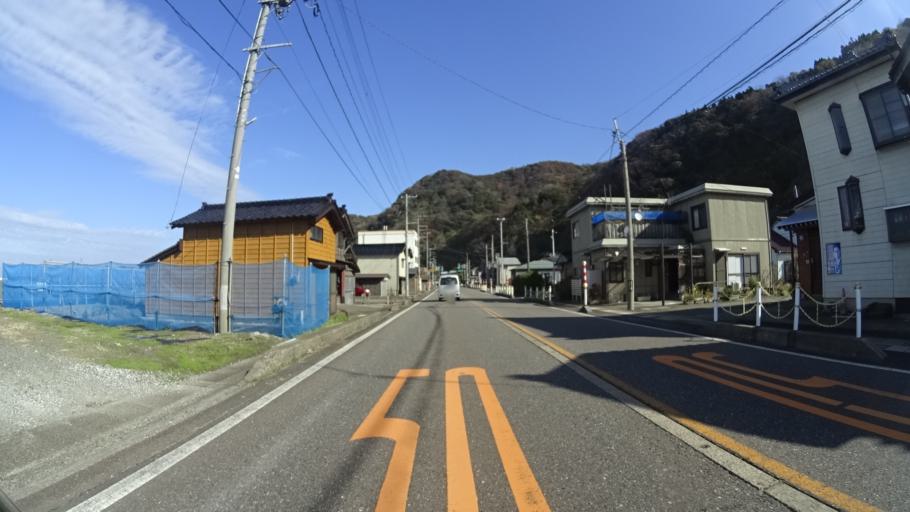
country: JP
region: Niigata
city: Itoigawa
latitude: 37.0735
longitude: 137.9373
